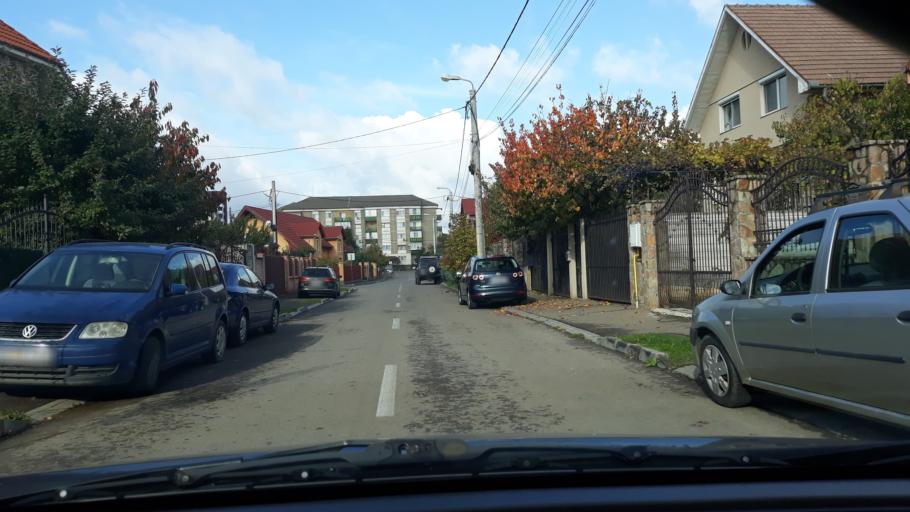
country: RO
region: Bihor
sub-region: Comuna Sanmartin
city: Sanmartin
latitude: 47.0289
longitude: 21.9495
